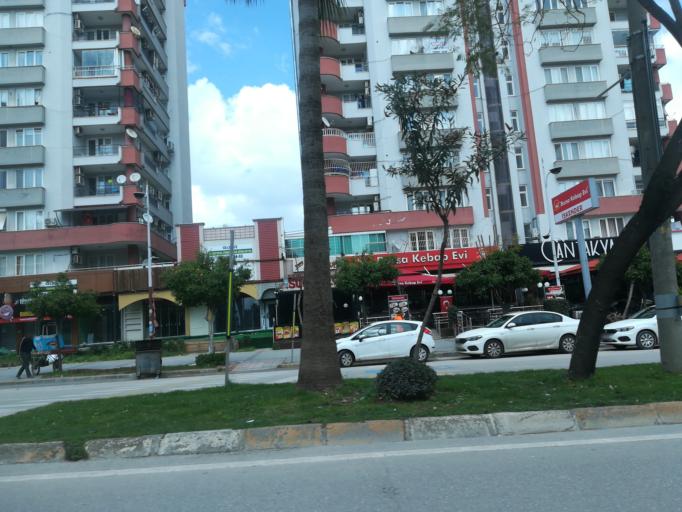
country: TR
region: Adana
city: Adana
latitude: 37.0430
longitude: 35.3118
